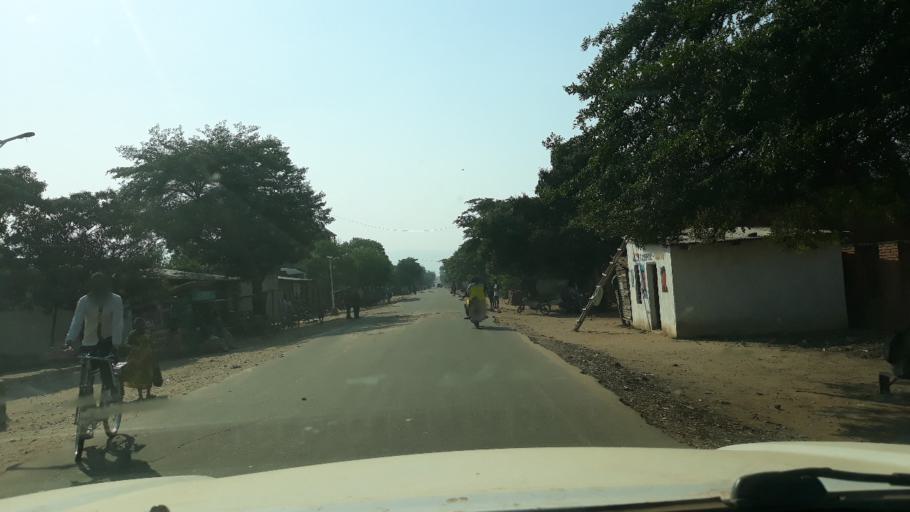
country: BI
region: Cibitoke
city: Cibitoke
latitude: -2.8558
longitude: 29.0278
